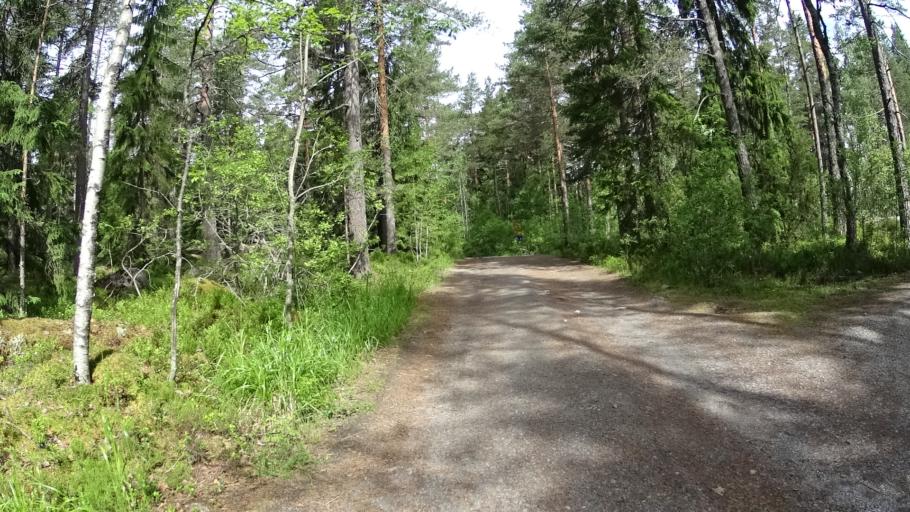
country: FI
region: Uusimaa
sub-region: Helsinki
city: Espoo
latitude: 60.2889
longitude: 24.5147
